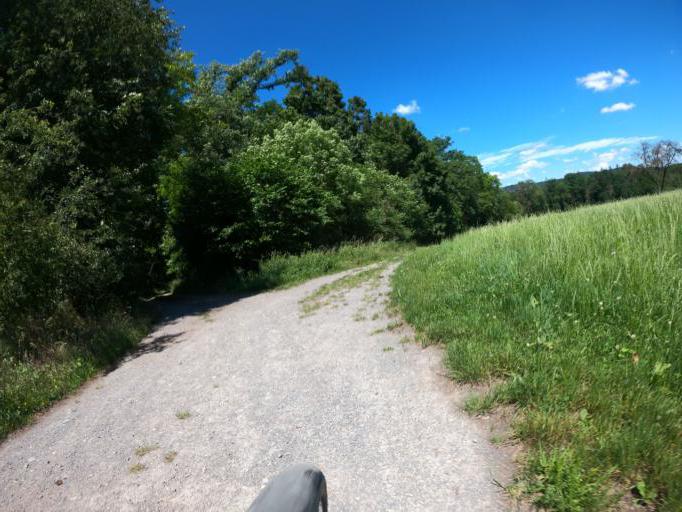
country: DE
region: Baden-Wuerttemberg
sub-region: Regierungsbezirk Stuttgart
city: Sersheim
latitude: 48.9756
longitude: 9.0161
